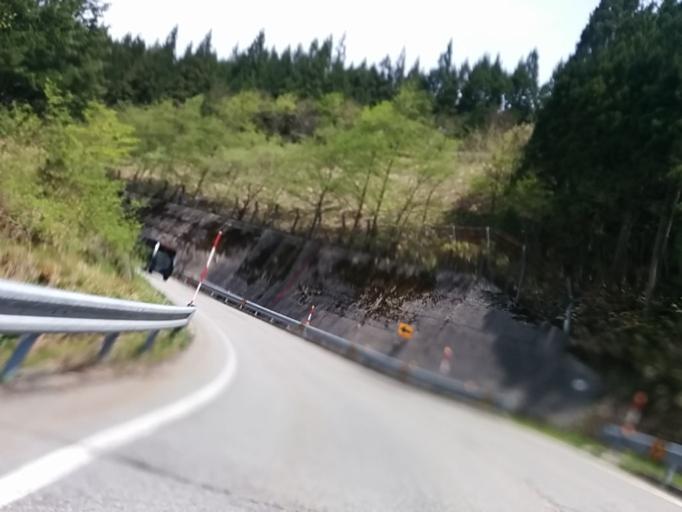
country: JP
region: Gifu
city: Takayama
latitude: 36.2301
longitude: 137.5308
